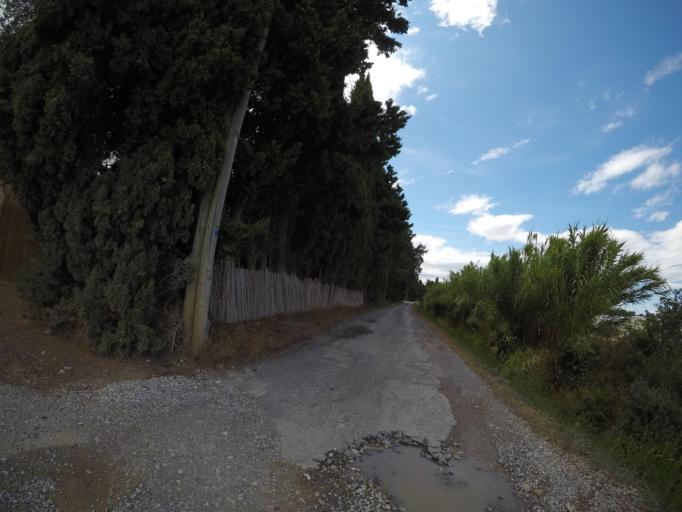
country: FR
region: Languedoc-Roussillon
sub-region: Departement des Pyrenees-Orientales
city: Villeneuve-la-Riviere
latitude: 42.6994
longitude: 2.7880
